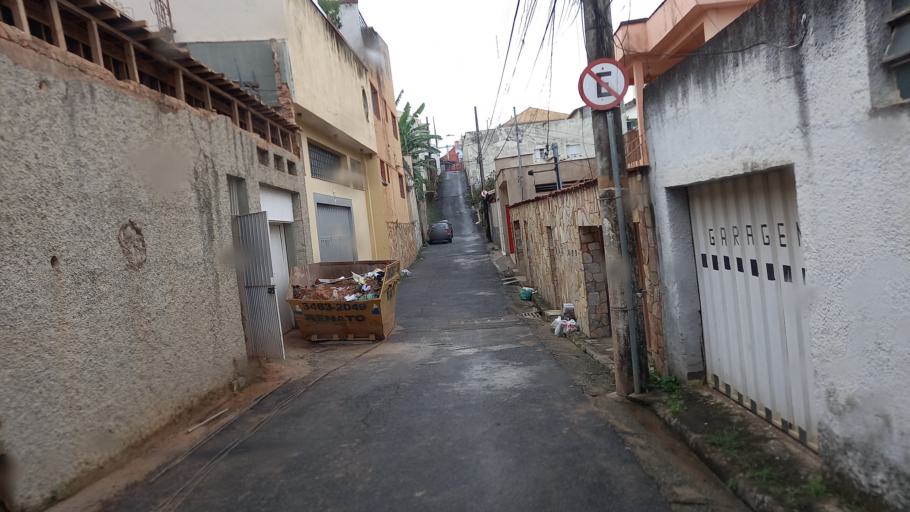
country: BR
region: Minas Gerais
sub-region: Belo Horizonte
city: Belo Horizonte
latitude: -19.9123
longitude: -43.9133
